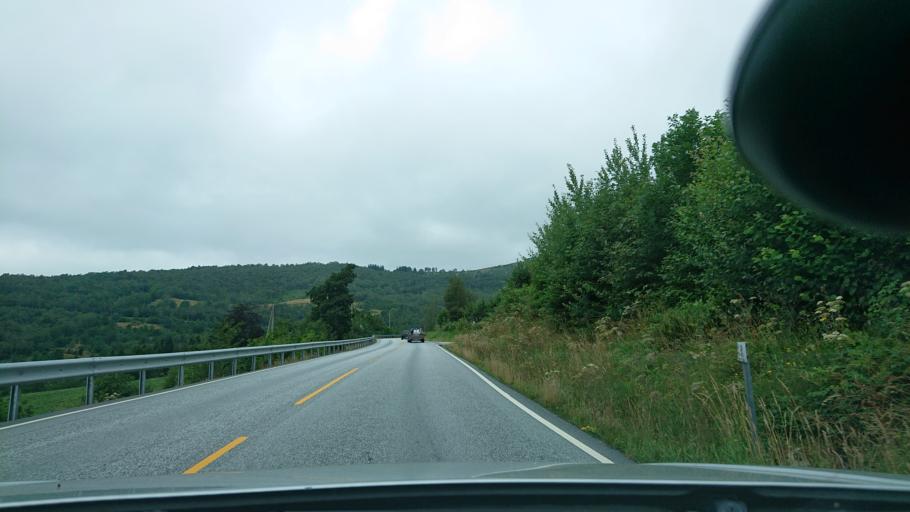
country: NO
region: Rogaland
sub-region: Hjelmeland
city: Hjelmelandsvagen
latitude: 59.1687
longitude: 6.1713
